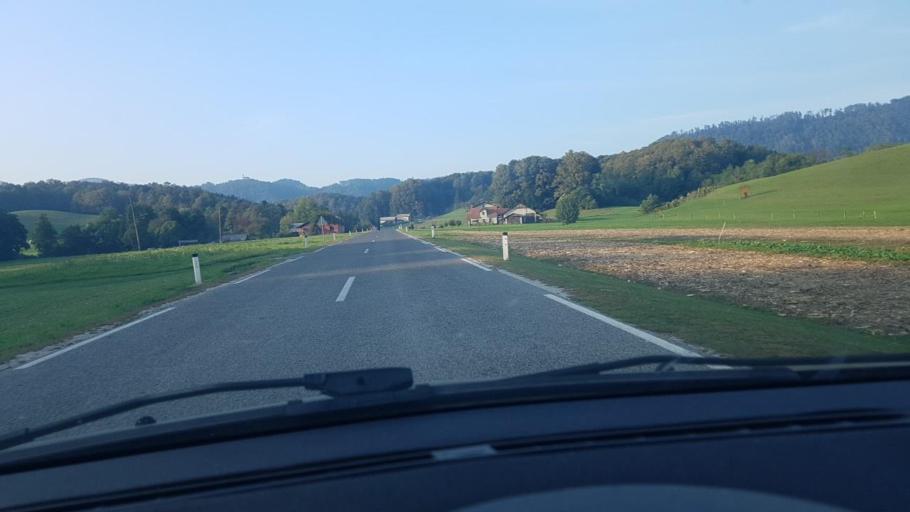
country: SI
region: Rogatec
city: Rogatec
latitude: 46.2410
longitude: 15.7018
